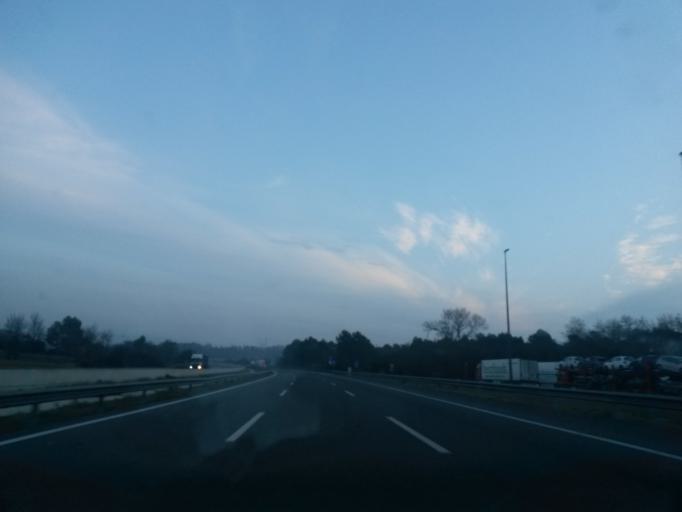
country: ES
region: Catalonia
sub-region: Provincia de Girona
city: Pontos
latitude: 42.1738
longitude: 2.9312
